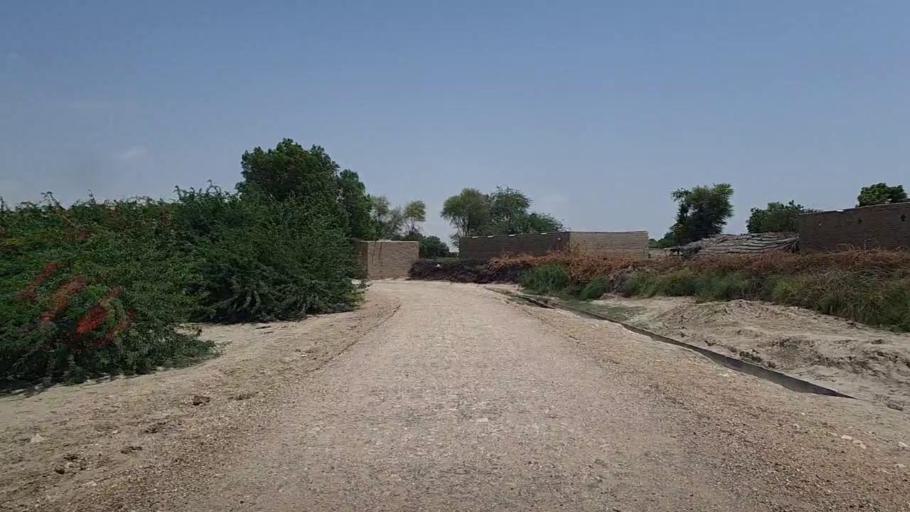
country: PK
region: Sindh
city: Pad Idan
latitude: 26.7381
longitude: 68.3103
